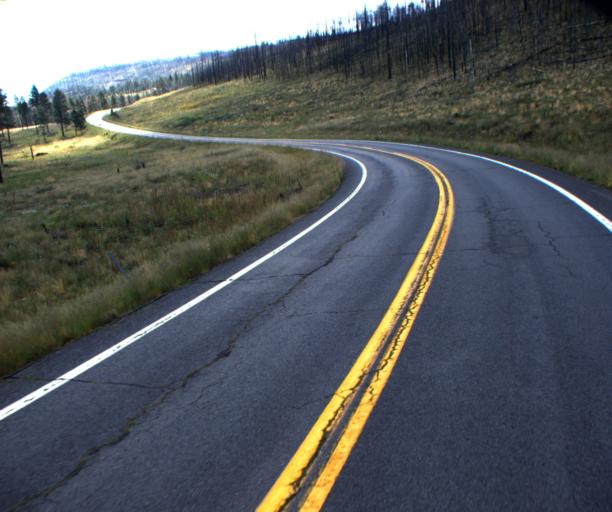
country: US
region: Arizona
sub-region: Apache County
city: Eagar
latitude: 34.0547
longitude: -109.3526
